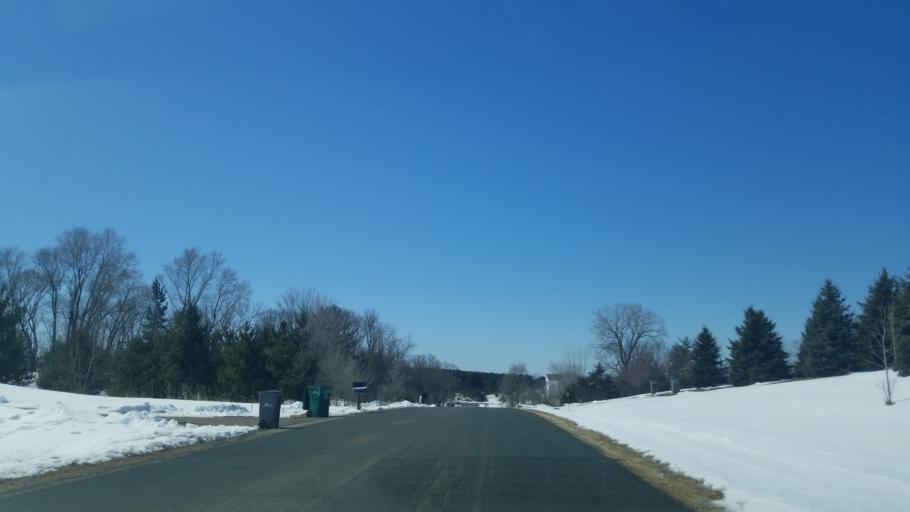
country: US
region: Wisconsin
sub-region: Saint Croix County
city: Roberts
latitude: 44.9941
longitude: -92.6559
